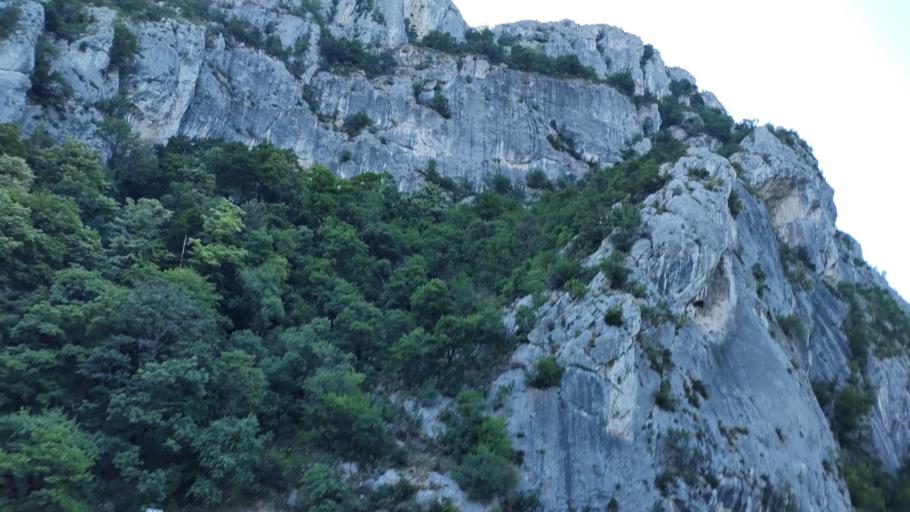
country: RO
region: Mehedinti
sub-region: Comuna Dubova
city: Dubova
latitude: 44.5929
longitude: 22.2607
